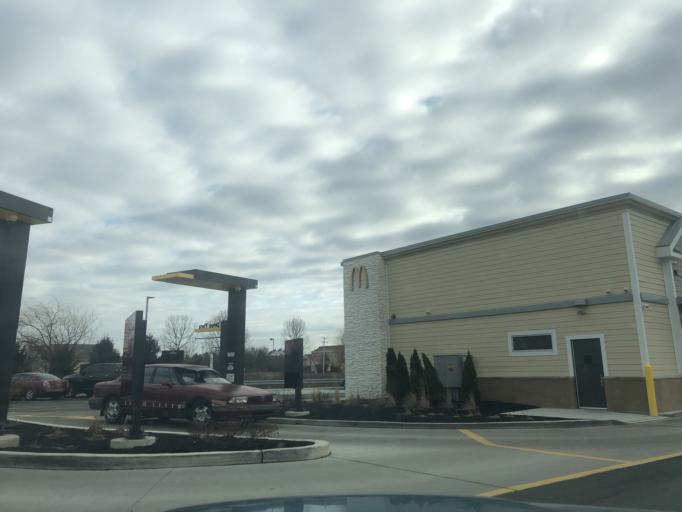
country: US
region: Pennsylvania
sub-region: Bucks County
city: Spinnerstown
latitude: 40.4359
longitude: -75.4186
